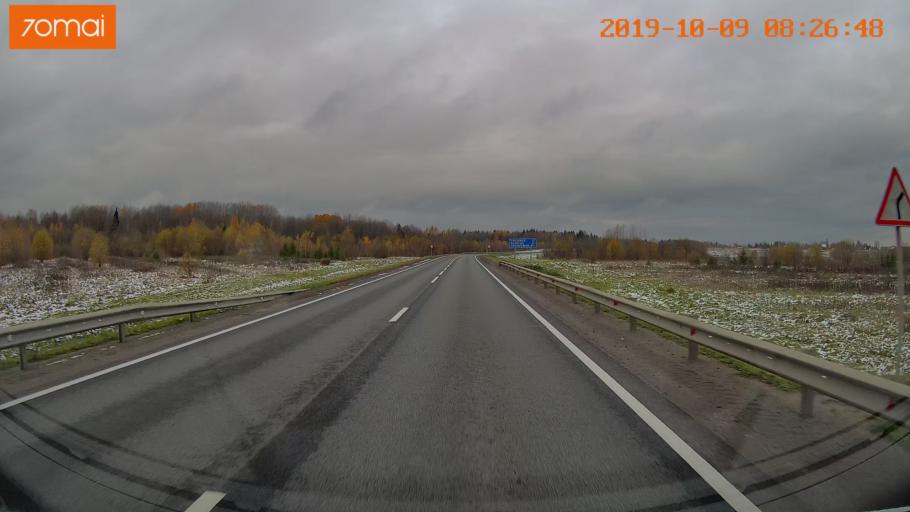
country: RU
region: Vologda
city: Gryazovets
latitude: 58.7969
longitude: 40.2600
